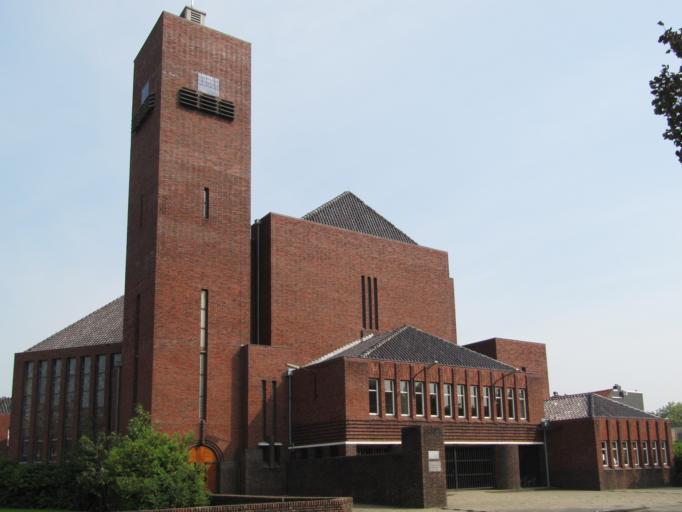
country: NL
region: Friesland
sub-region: Gemeente Leeuwarden
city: Bilgaard
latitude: 53.2052
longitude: 5.7854
